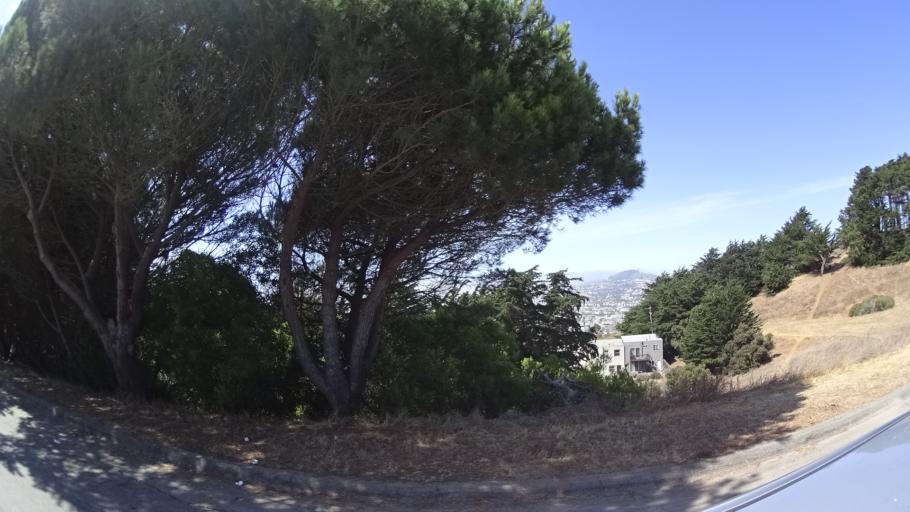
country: US
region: California
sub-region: San Mateo County
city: Daly City
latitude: 37.7217
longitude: -122.4239
